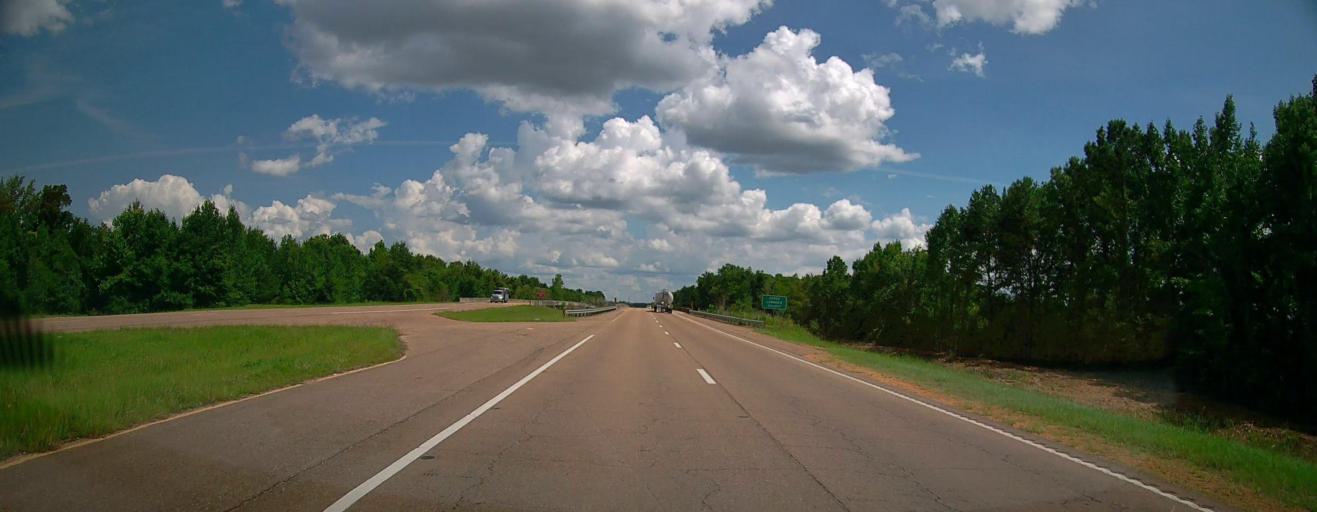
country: US
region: Mississippi
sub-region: Lowndes County
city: Columbus Air Force Base
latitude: 33.6757
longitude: -88.4304
